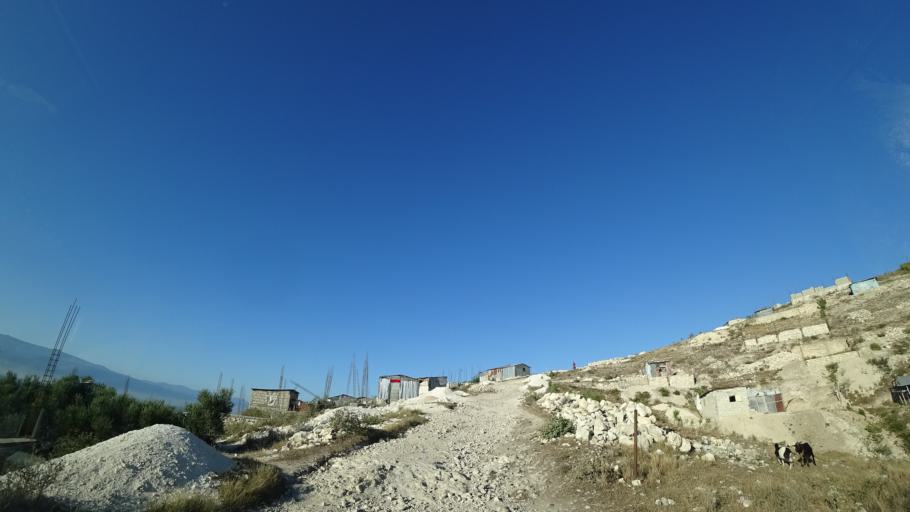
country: HT
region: Ouest
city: Croix des Bouquets
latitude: 18.6698
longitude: -72.2455
